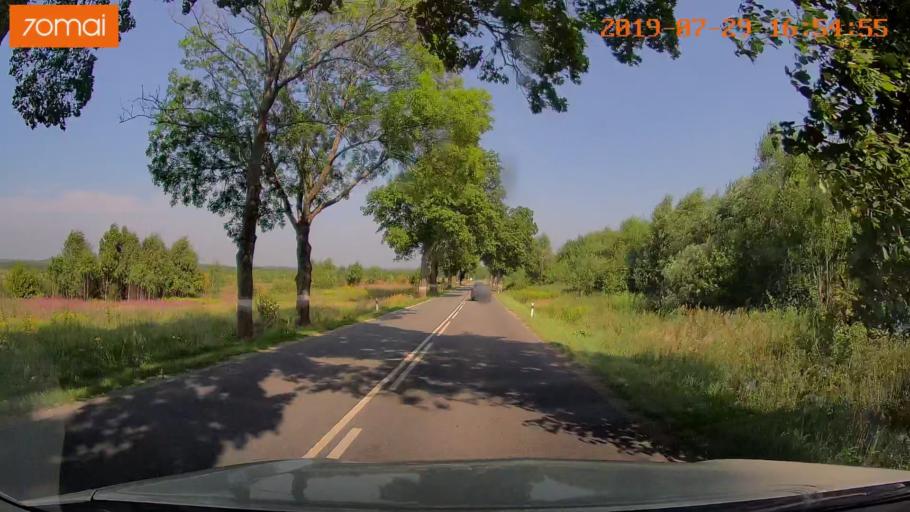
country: RU
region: Kaliningrad
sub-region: Gorod Svetlogorsk
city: Svetlogorsk
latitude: 54.8129
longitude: 20.1409
